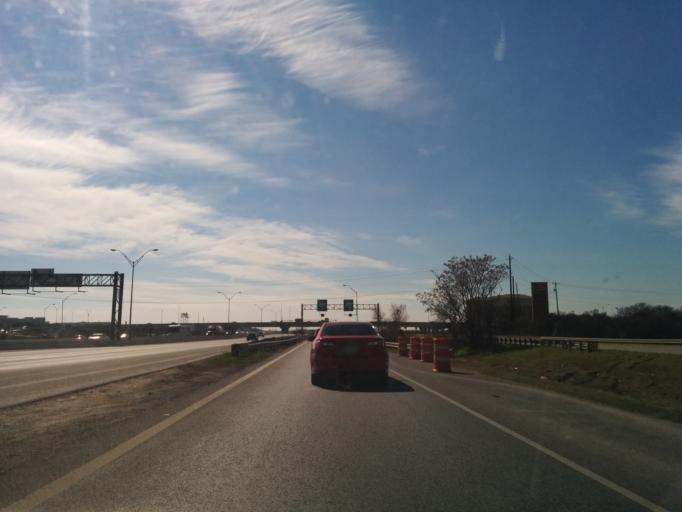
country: US
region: Texas
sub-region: Bexar County
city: Shavano Park
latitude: 29.5945
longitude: -98.5993
